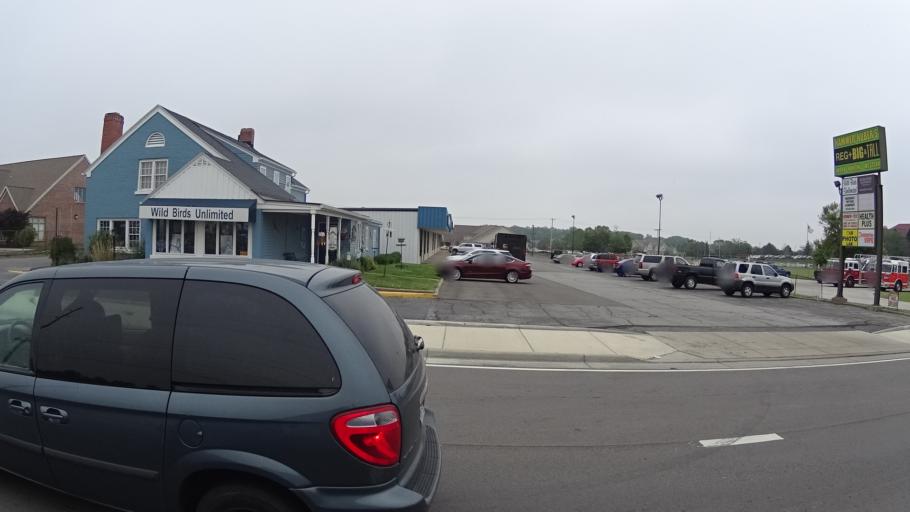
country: US
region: Ohio
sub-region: Erie County
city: Sandusky
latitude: 41.4140
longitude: -82.6698
